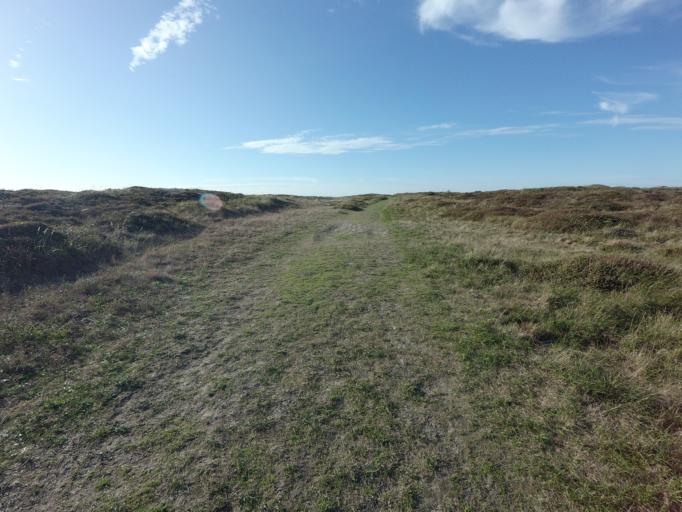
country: NL
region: North Holland
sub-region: Gemeente Den Helder
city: Den Helder
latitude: 53.0171
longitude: 4.7272
